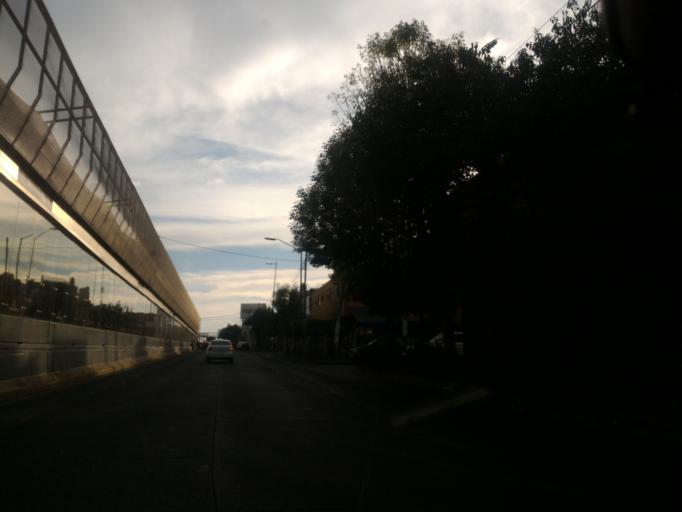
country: MX
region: Jalisco
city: Guadalajara
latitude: 20.6437
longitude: -103.3725
